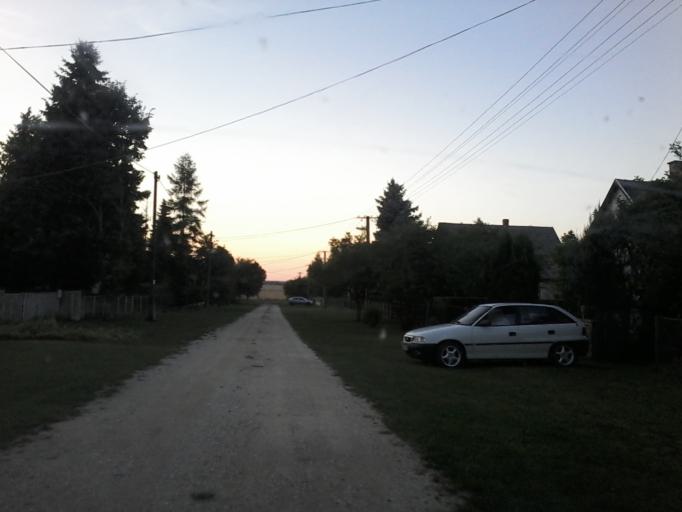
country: HU
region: Vas
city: Janoshaza
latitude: 47.1621
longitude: 17.0969
